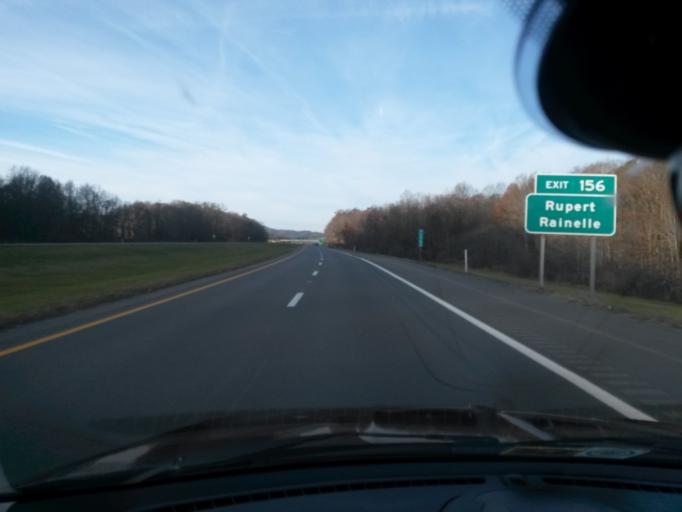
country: US
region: West Virginia
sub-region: Greenbrier County
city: Rainelle
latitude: 37.9077
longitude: -80.6186
